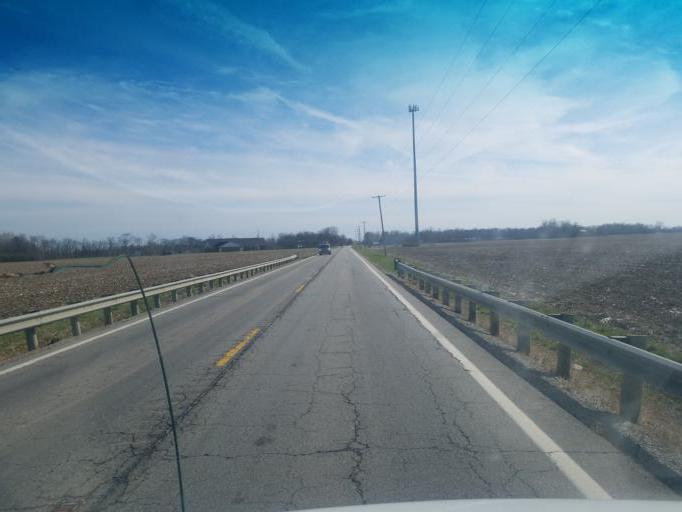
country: US
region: Ohio
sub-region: Union County
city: Richwood
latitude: 40.3985
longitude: -83.2667
